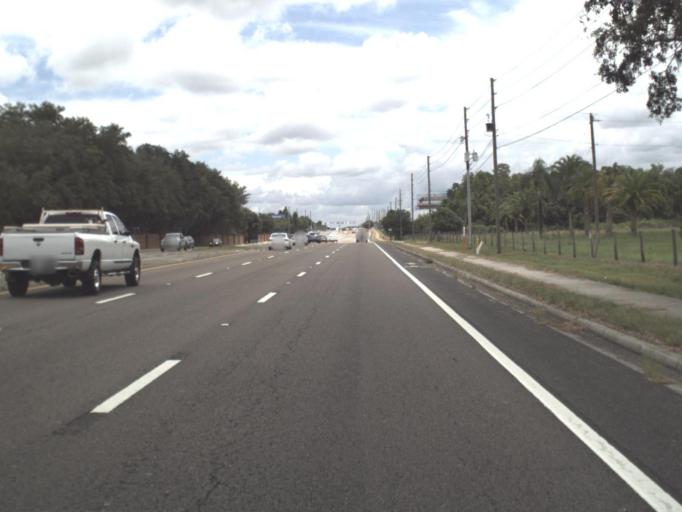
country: US
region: Florida
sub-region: Pasco County
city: Trinity
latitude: 28.2059
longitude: -82.6740
